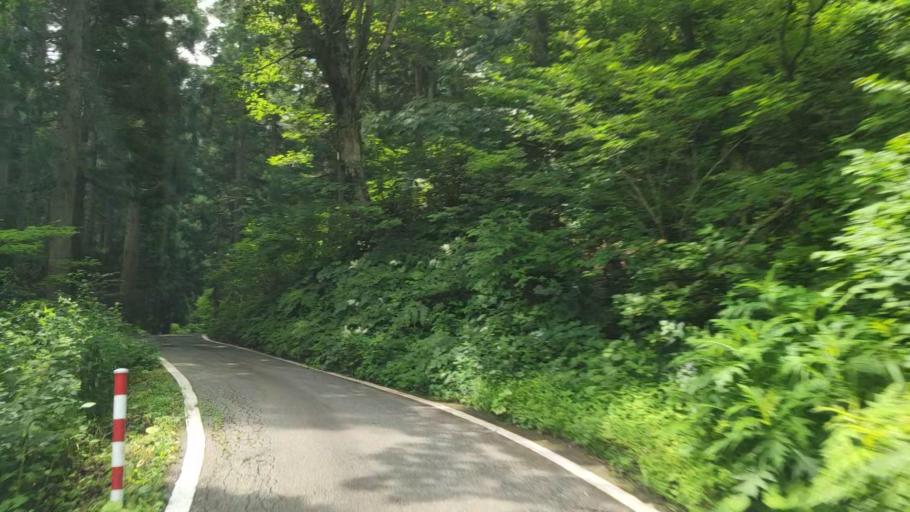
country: JP
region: Fukui
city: Katsuyama
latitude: 36.1814
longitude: 136.5239
